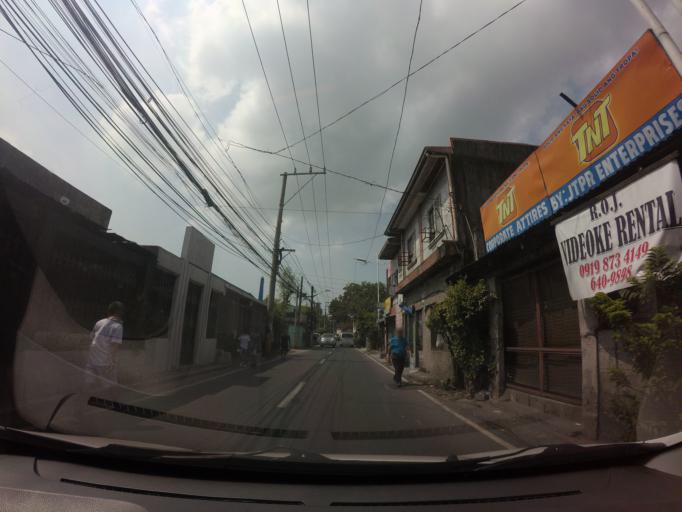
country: PH
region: Calabarzon
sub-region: Province of Rizal
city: Taguig
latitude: 14.5286
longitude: 121.0732
